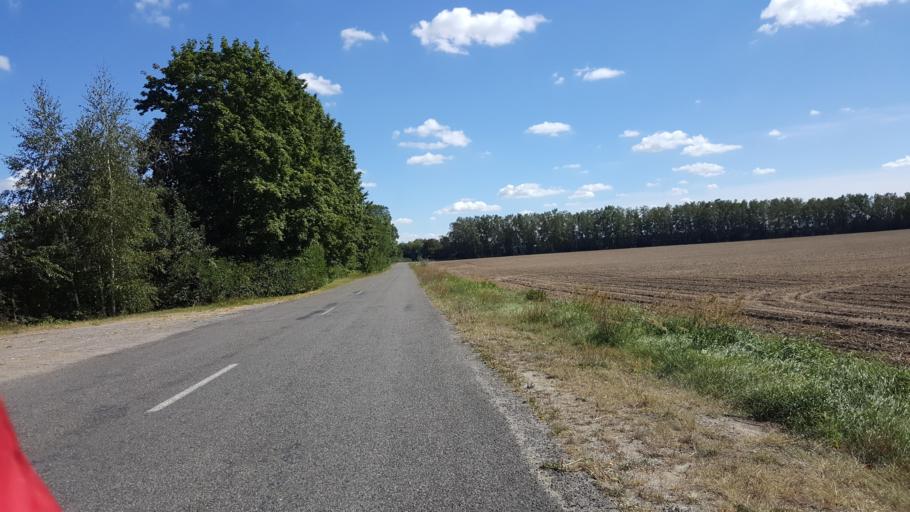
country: BY
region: Brest
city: Vysokaye
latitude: 52.2762
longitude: 23.3597
